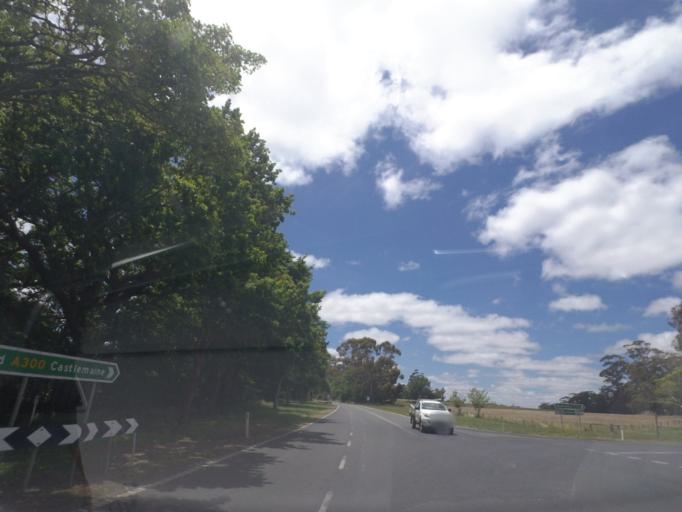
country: AU
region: Victoria
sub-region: Mount Alexander
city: Castlemaine
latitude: -37.3351
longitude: 144.1651
